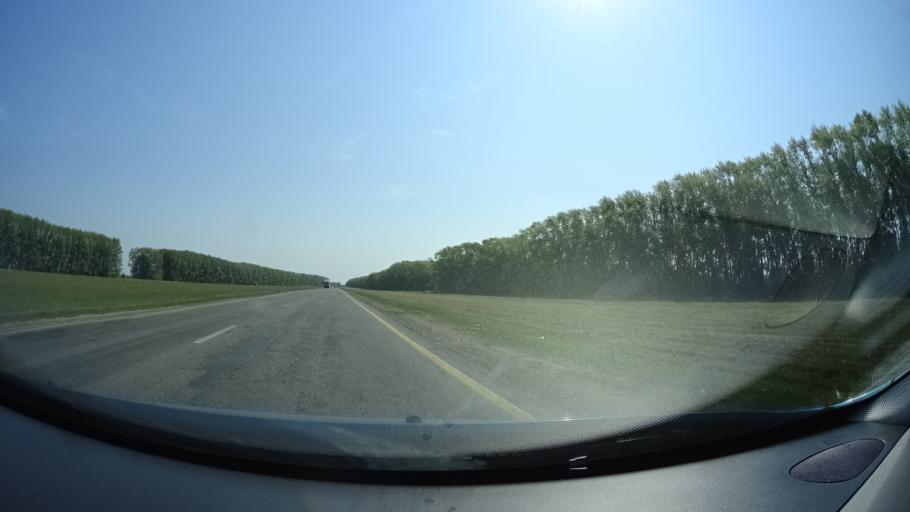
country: RU
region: Bashkortostan
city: Karmaskaly
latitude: 54.3950
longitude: 56.1100
